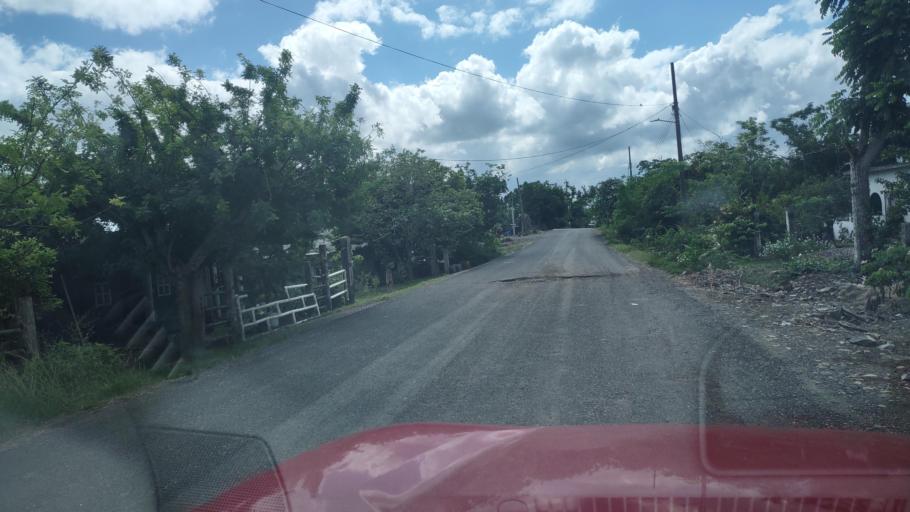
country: MX
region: Puebla
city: San Jose Acateno
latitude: 20.2720
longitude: -97.1295
